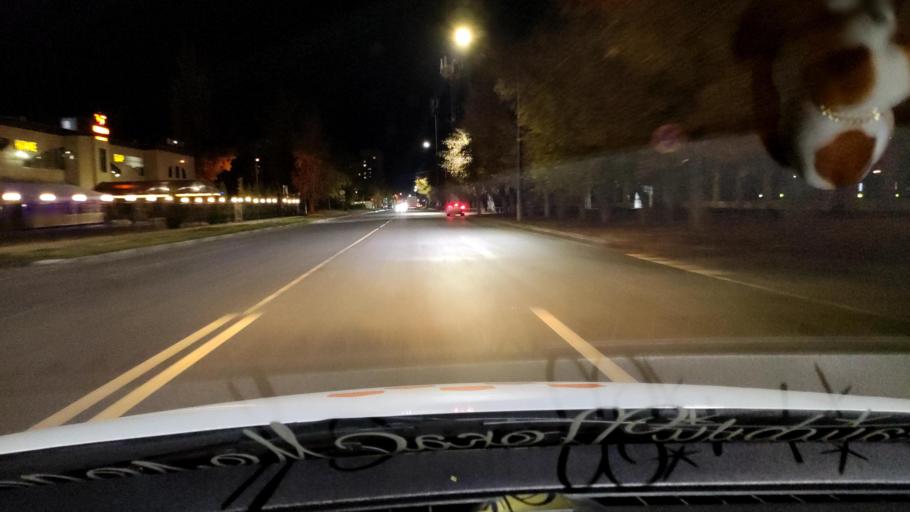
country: RU
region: Voronezj
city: Voronezh
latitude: 51.6425
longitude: 39.1783
